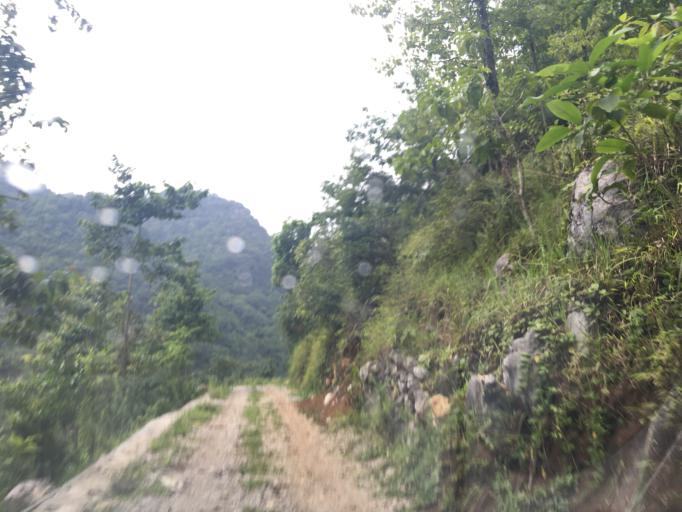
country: CN
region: Guangxi Zhuangzu Zizhiqu
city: Xinzhou
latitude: 25.2218
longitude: 105.6284
